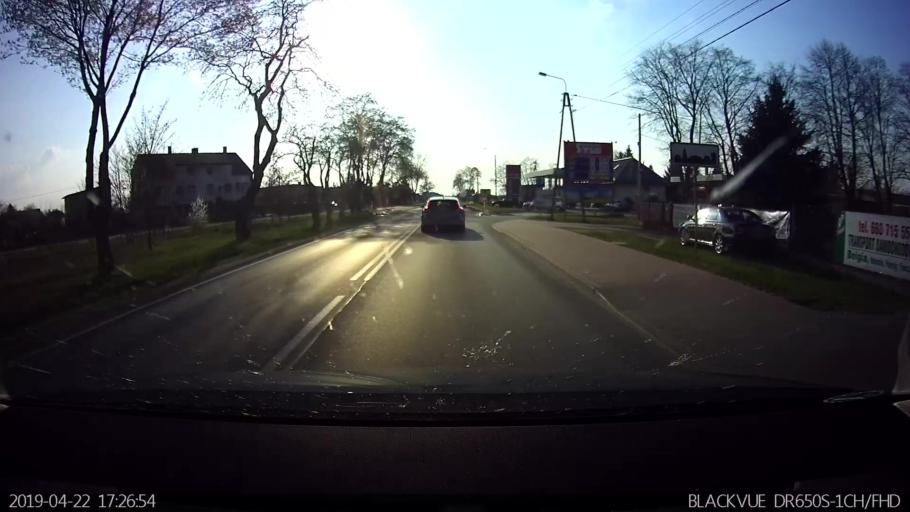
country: PL
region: Masovian Voivodeship
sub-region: Powiat sokolowski
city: Sokolow Podlaski
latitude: 52.3955
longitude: 22.2707
